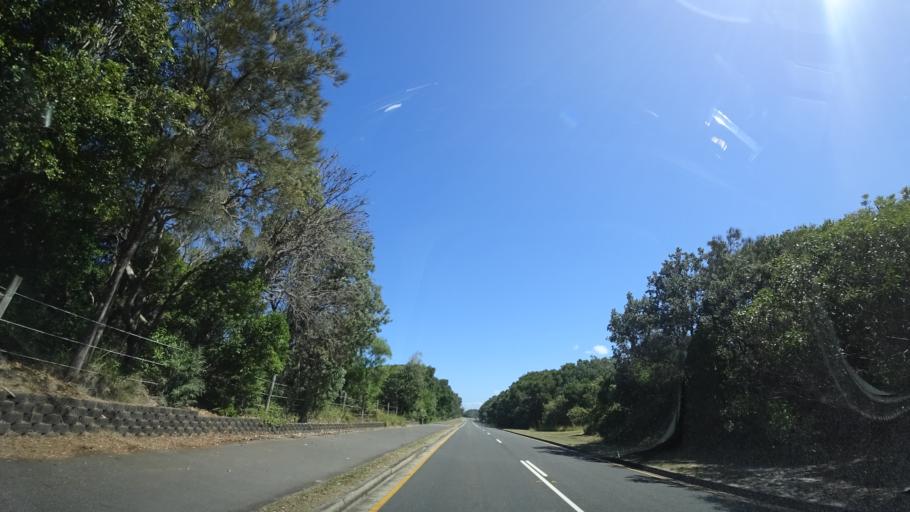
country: AU
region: Queensland
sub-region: Sunshine Coast
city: Mooloolaba
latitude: -26.6195
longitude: 153.1007
